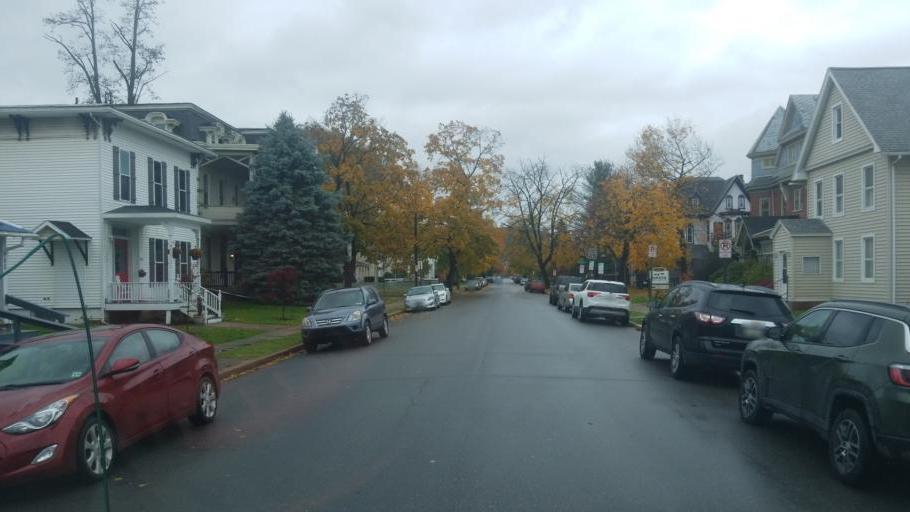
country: US
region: Pennsylvania
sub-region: Clinton County
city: Lock Haven
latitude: 41.1369
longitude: -77.4502
